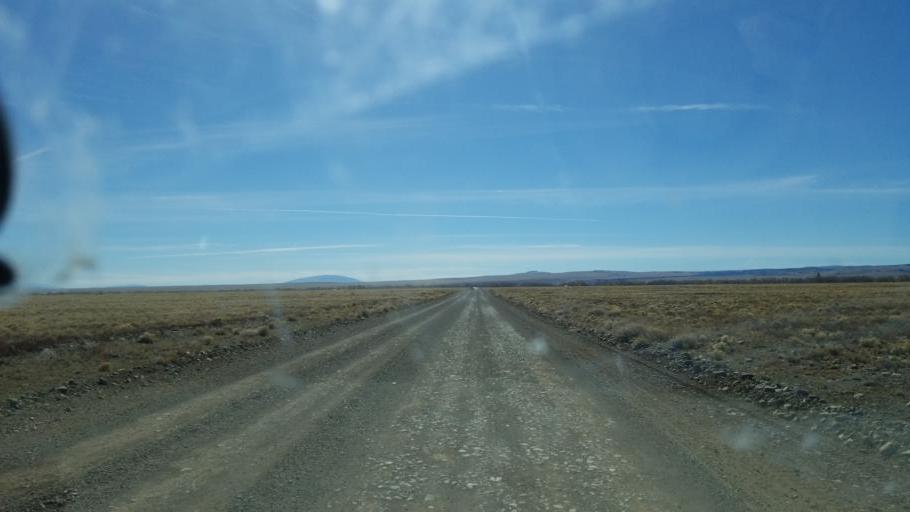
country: US
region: Colorado
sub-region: Rio Grande County
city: Monte Vista
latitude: 37.3257
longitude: -106.1488
